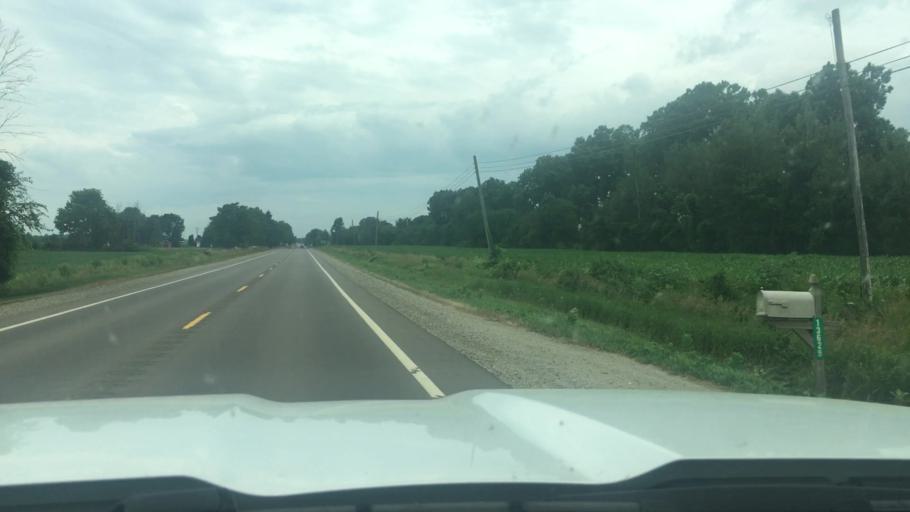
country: US
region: Michigan
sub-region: Clinton County
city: Fowler
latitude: 43.0019
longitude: -84.7915
